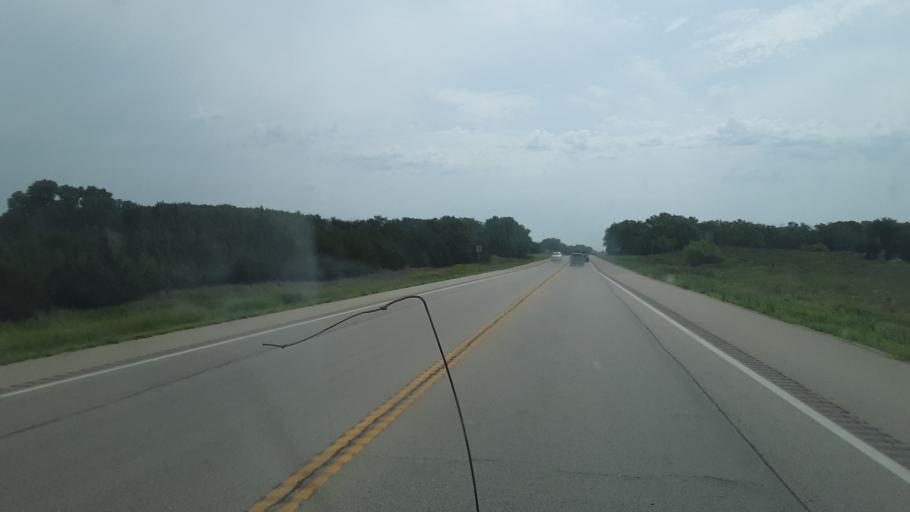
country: US
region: Kansas
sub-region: Rice County
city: Sterling
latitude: 37.9851
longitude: -98.2744
